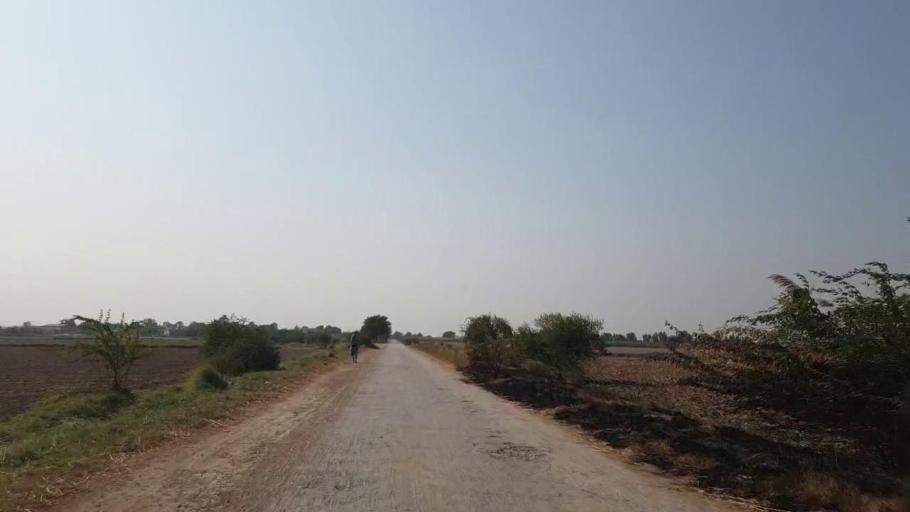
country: PK
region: Sindh
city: Bulri
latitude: 24.9559
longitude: 68.3462
